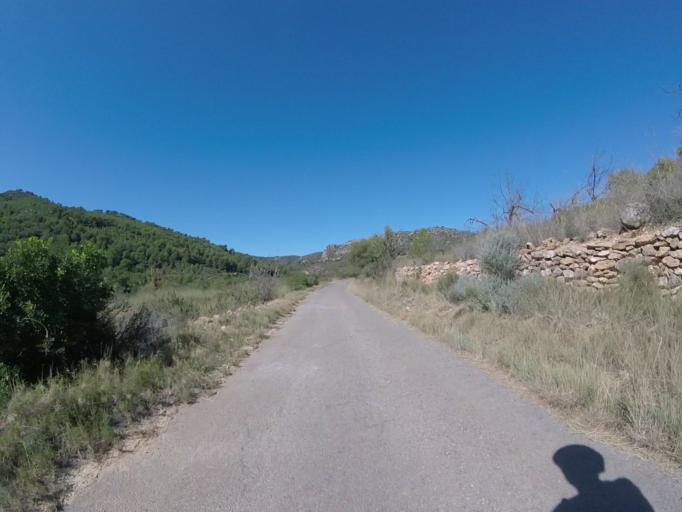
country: ES
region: Valencia
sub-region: Provincia de Castello
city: Orpesa/Oropesa del Mar
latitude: 40.1371
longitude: 0.1039
